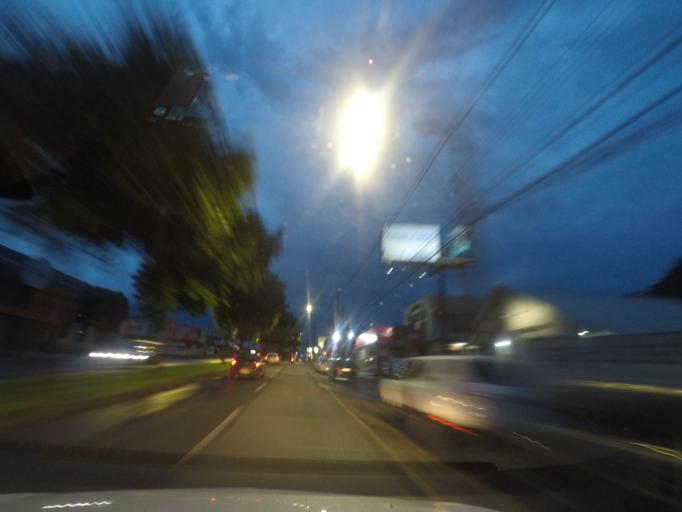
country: BR
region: Goias
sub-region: Goiania
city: Goiania
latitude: -16.7092
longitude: -49.3191
